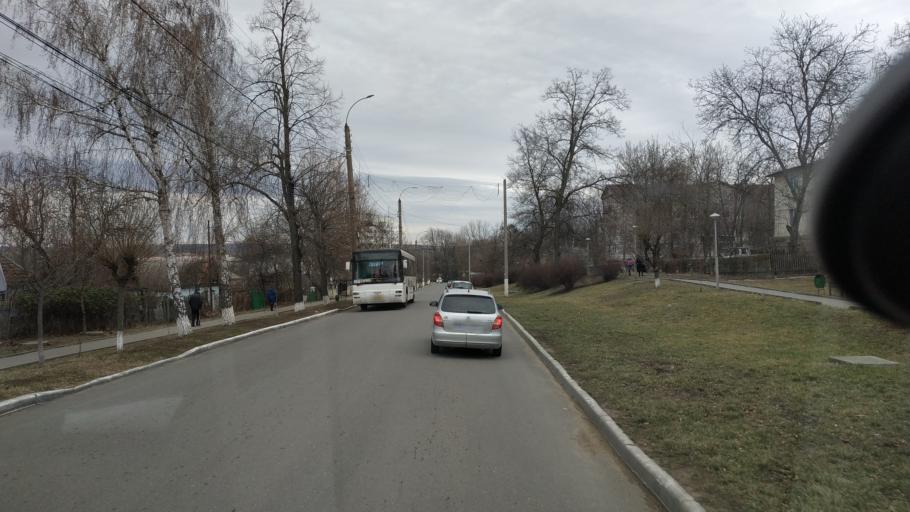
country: MD
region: Chisinau
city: Vadul lui Voda
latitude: 47.0870
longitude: 29.0819
